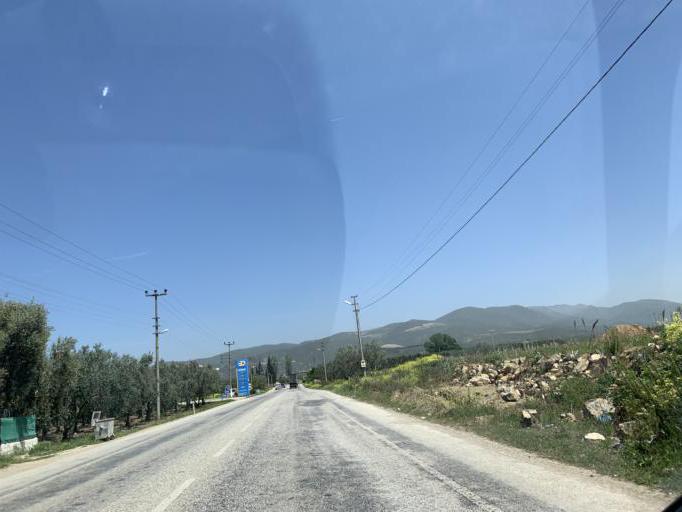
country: TR
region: Bursa
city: Iznik
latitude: 40.4184
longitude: 29.7161
